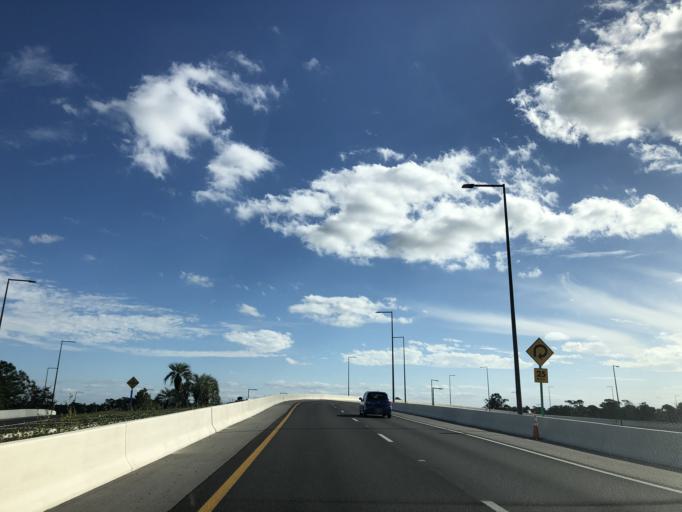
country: US
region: Florida
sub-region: Osceola County
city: Celebration
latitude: 28.3488
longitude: -81.5511
